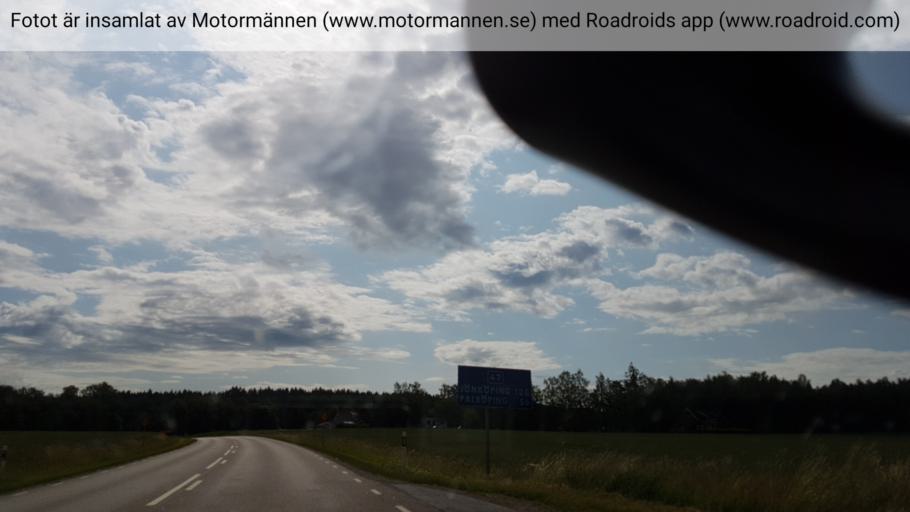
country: SE
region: Vaestra Goetaland
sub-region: Grastorps Kommun
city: Graestorp
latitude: 58.3294
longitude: 12.6948
